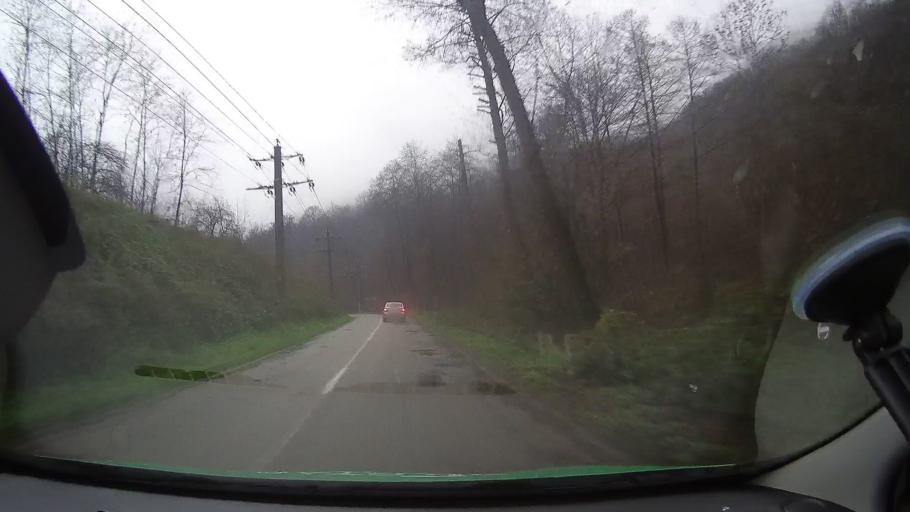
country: RO
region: Arad
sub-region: Comuna Dezna
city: Dezna
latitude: 46.4134
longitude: 22.2547
